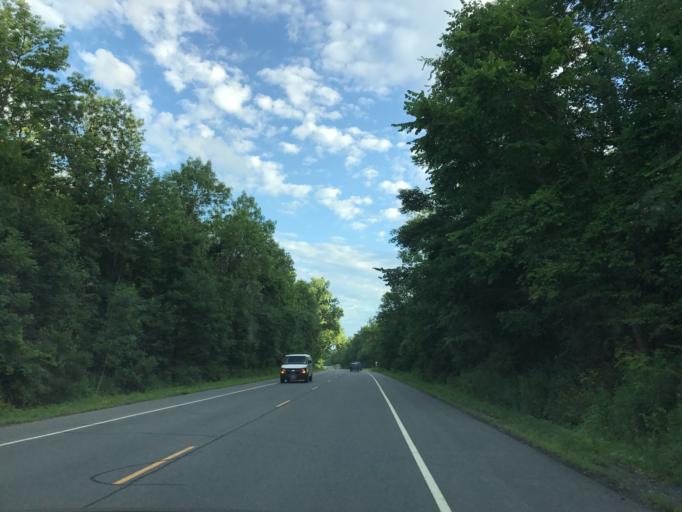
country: US
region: New York
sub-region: Saratoga County
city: Schuylerville
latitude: 43.0401
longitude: -73.5926
